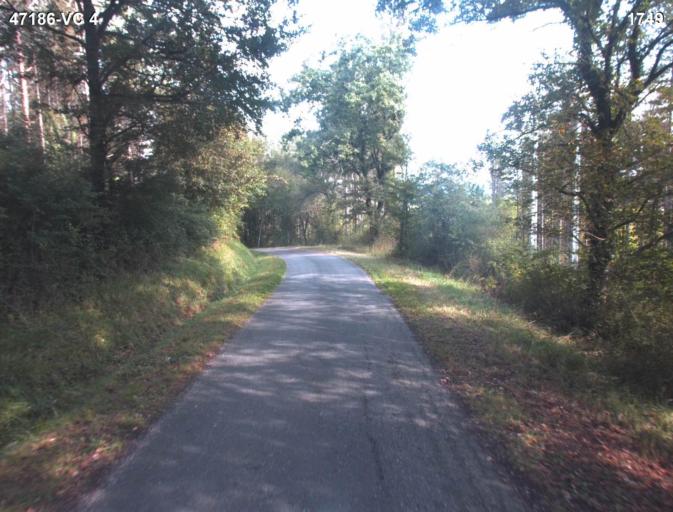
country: FR
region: Aquitaine
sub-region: Departement du Lot-et-Garonne
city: Port-Sainte-Marie
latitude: 44.2001
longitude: 0.4355
